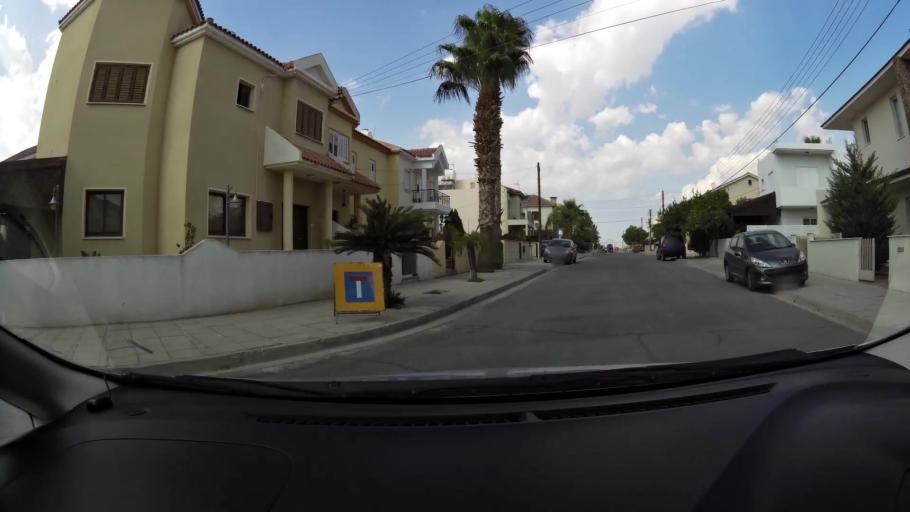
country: CY
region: Larnaka
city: Dhromolaxia
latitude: 34.9068
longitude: 33.5911
